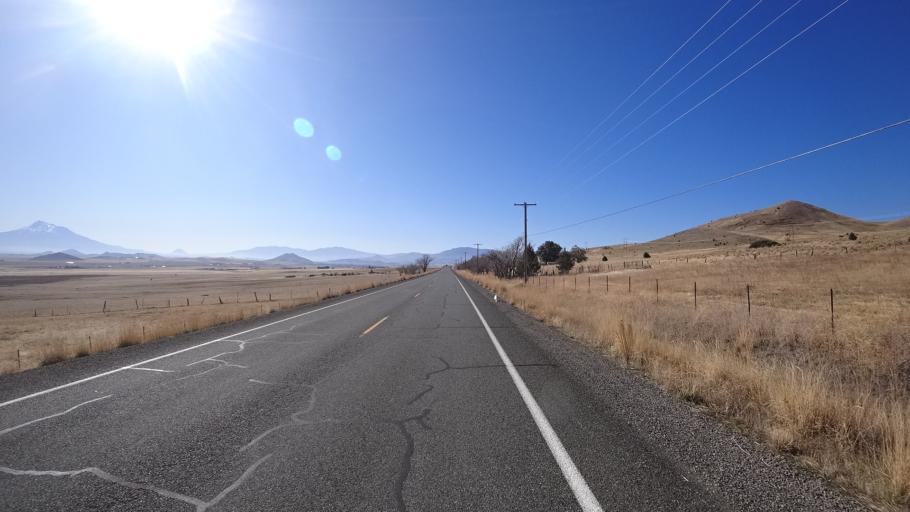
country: US
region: California
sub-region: Siskiyou County
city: Montague
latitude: 41.7869
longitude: -122.5171
